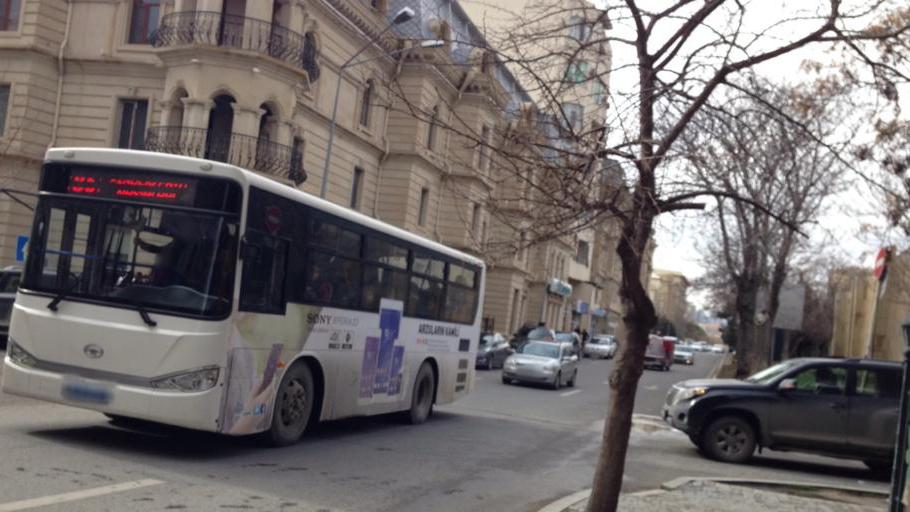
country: AZ
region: Baki
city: Baku
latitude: 40.3911
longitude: 49.8410
